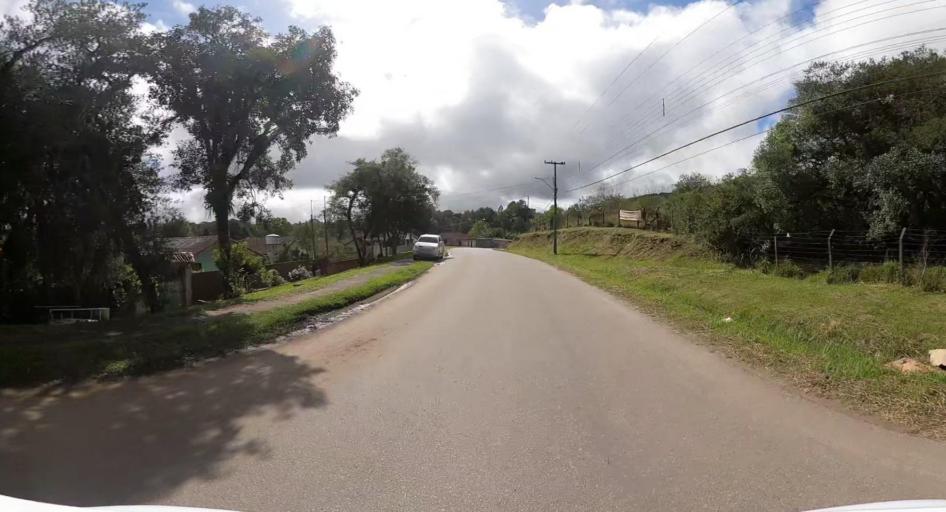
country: BR
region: Parana
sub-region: Campina Grande Do Sul
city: Campina Grande do Sul
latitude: -25.3020
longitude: -49.0484
